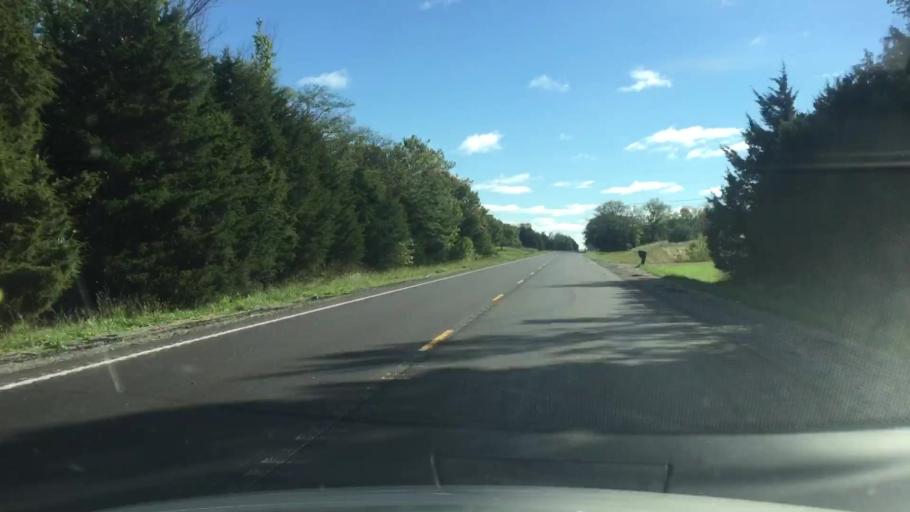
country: US
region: Missouri
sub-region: Boone County
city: Columbia
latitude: 38.9897
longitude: -92.5136
